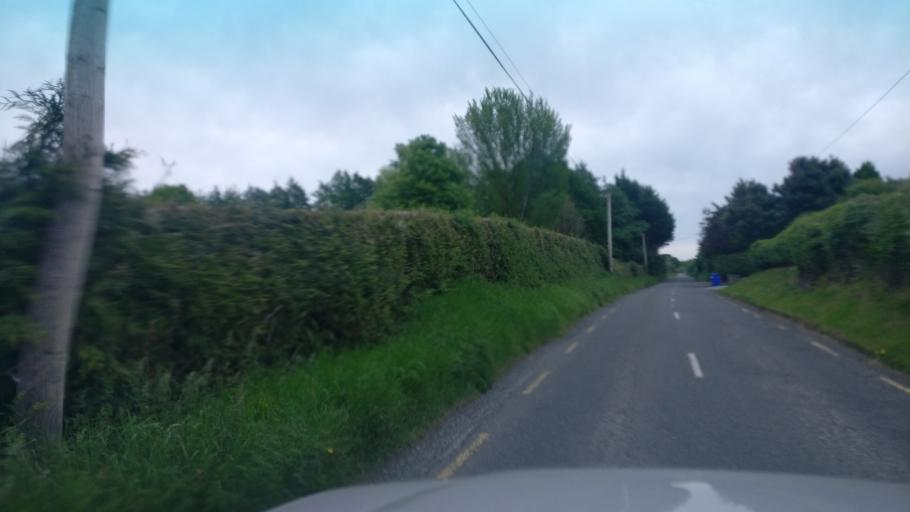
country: IE
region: Connaught
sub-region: County Galway
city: Portumna
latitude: 53.1003
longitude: -8.2499
